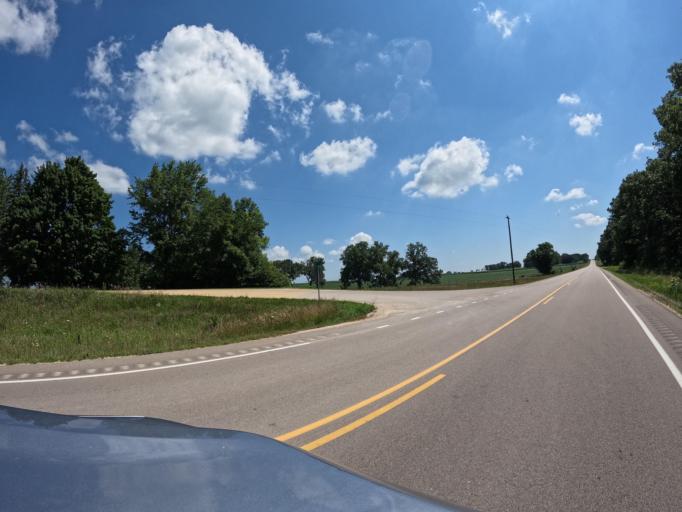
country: US
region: Iowa
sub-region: Clinton County
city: De Witt
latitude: 41.7577
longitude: -90.4296
